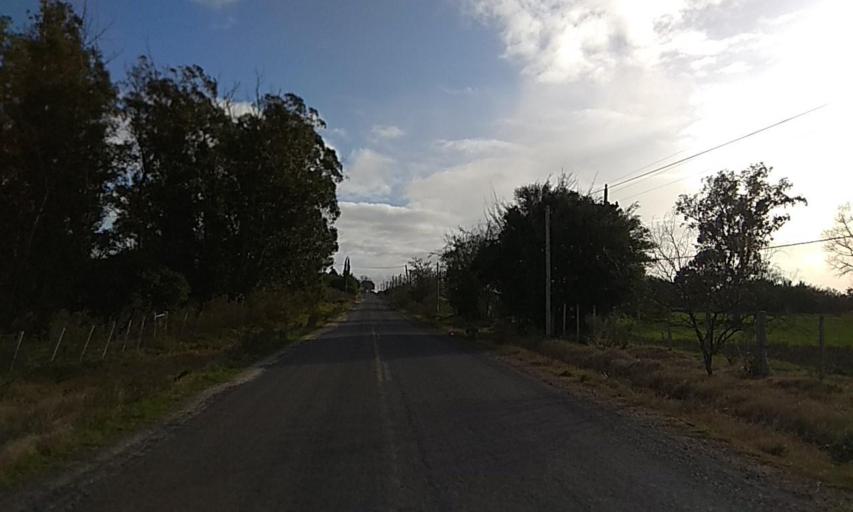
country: UY
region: Florida
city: Florida
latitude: -34.0488
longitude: -56.1893
